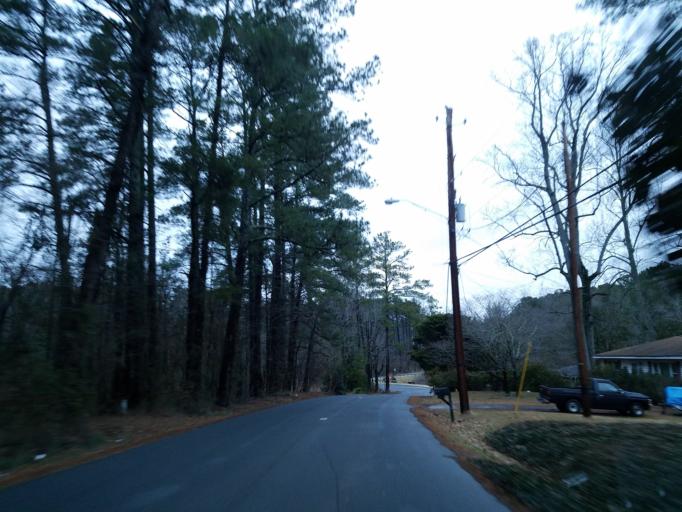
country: US
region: Georgia
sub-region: Cobb County
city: Acworth
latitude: 34.0679
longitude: -84.6604
